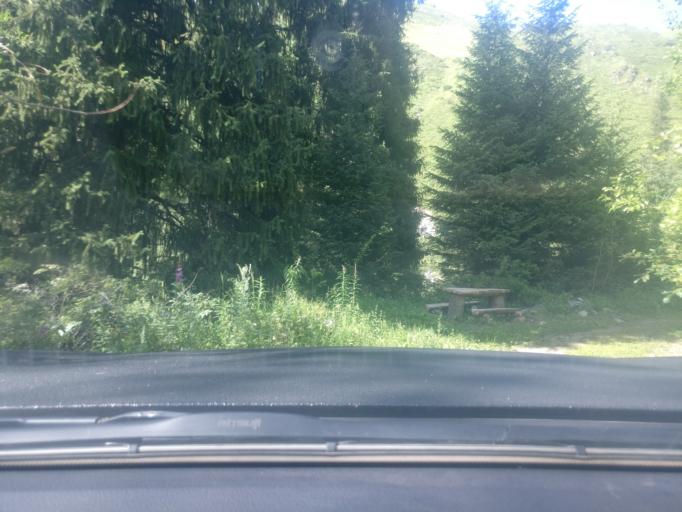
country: KZ
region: Almaty Qalasy
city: Almaty
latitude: 43.1059
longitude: 76.9527
